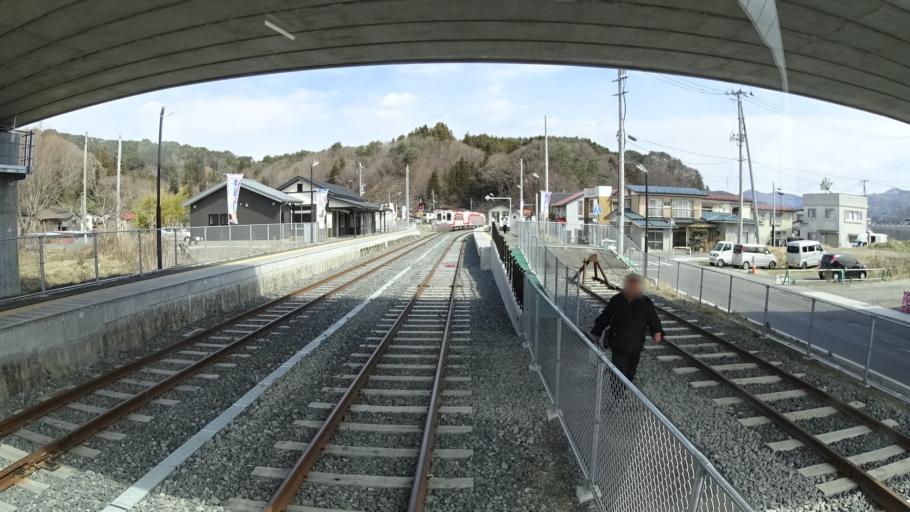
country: JP
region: Iwate
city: Miyako
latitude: 39.5811
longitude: 141.9376
